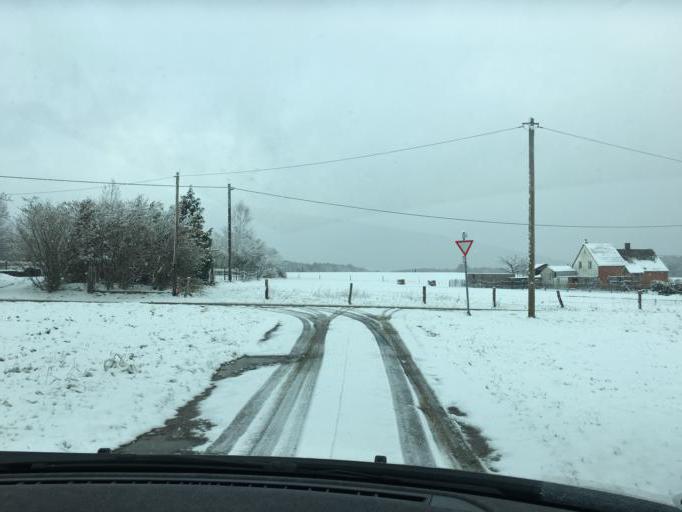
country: DE
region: North Rhine-Westphalia
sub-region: Regierungsbezirk Koln
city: Hurtgenwald
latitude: 50.7046
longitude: 6.4067
